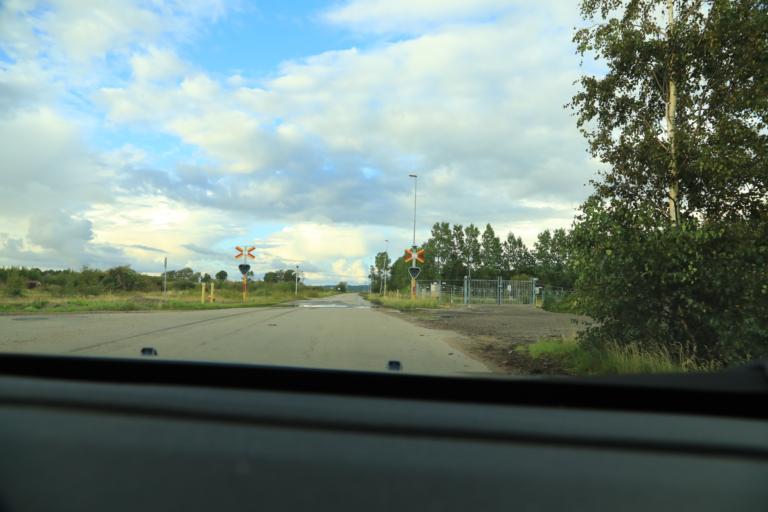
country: SE
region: Halland
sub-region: Varbergs Kommun
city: Varberg
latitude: 57.1197
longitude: 12.2433
